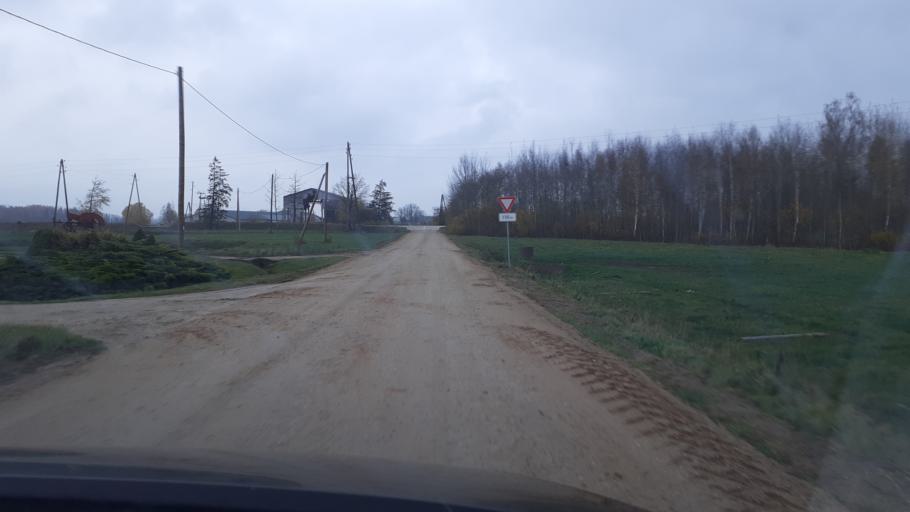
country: LV
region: Talsu Rajons
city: Sabile
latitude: 56.9414
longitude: 22.4205
